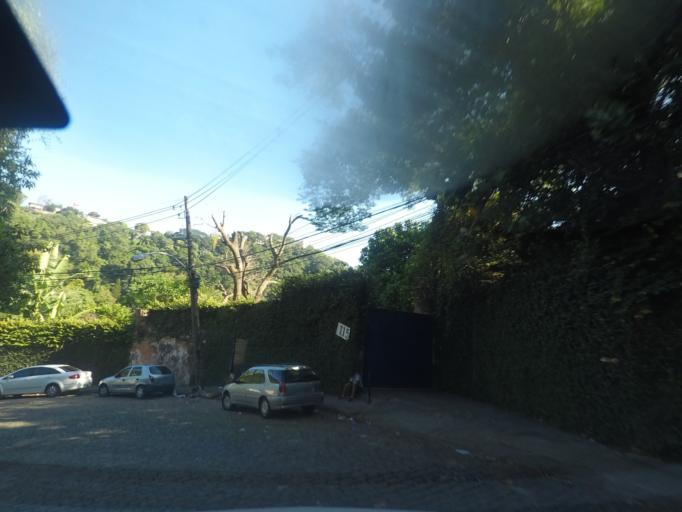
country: BR
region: Rio de Janeiro
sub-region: Rio De Janeiro
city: Rio de Janeiro
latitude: -22.9416
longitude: -43.2048
